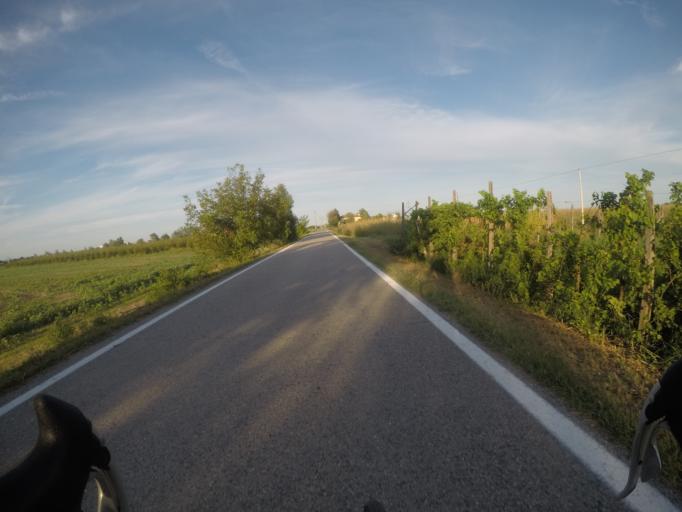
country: IT
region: Veneto
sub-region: Provincia di Rovigo
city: San Bellino
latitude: 45.0186
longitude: 11.5695
